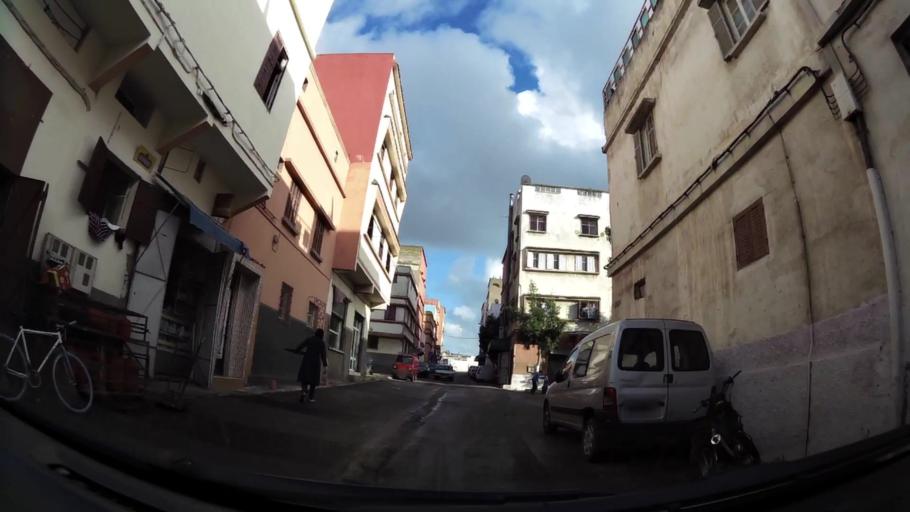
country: MA
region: Grand Casablanca
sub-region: Casablanca
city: Casablanca
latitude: 33.5499
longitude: -7.5927
